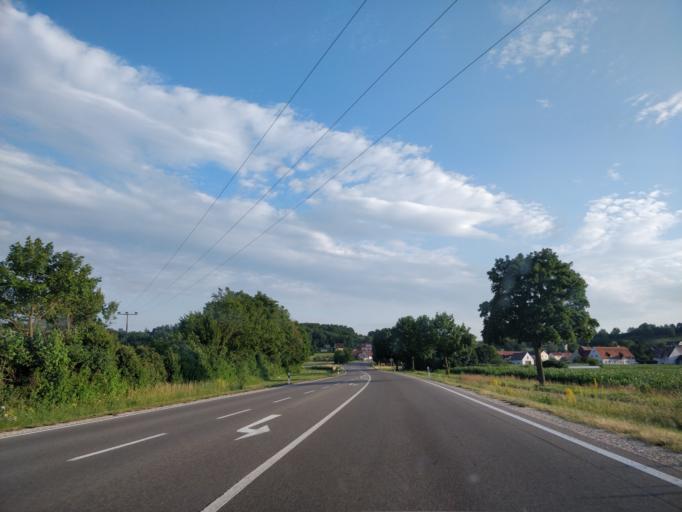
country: DE
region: Bavaria
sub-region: Swabia
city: Ederheim
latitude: 48.8263
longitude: 10.4650
